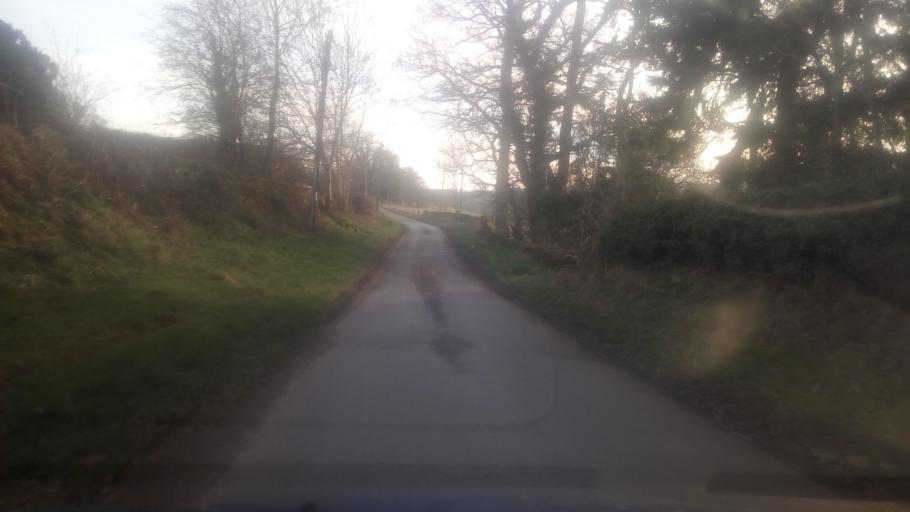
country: GB
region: Scotland
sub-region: The Scottish Borders
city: Jedburgh
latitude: 55.4546
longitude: -2.6327
